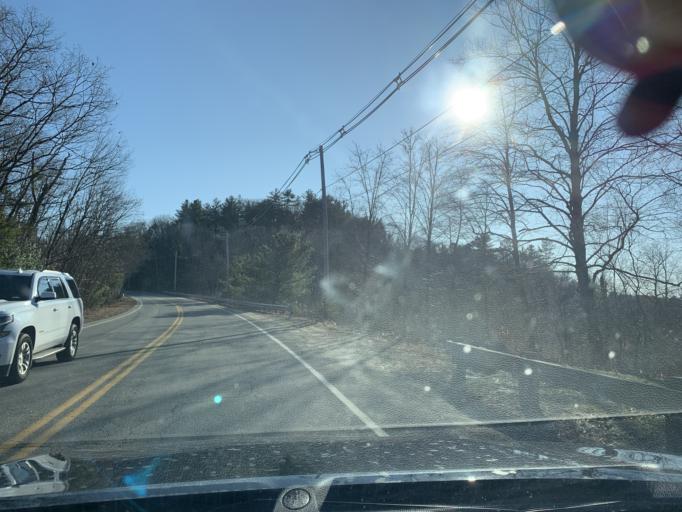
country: US
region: Massachusetts
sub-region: Essex County
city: Essex
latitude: 42.5966
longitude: -70.7676
